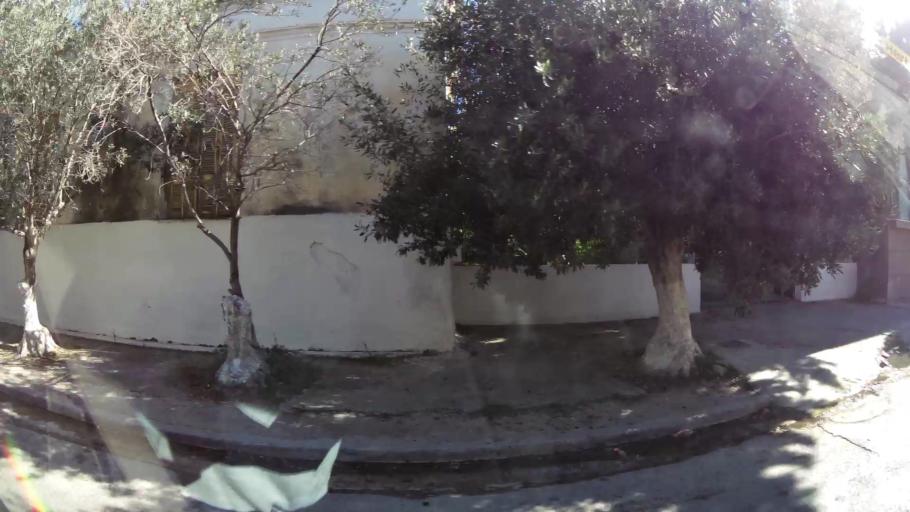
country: GR
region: Attica
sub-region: Nomarchia Anatolikis Attikis
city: Markopoulo
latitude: 37.8855
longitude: 23.9382
